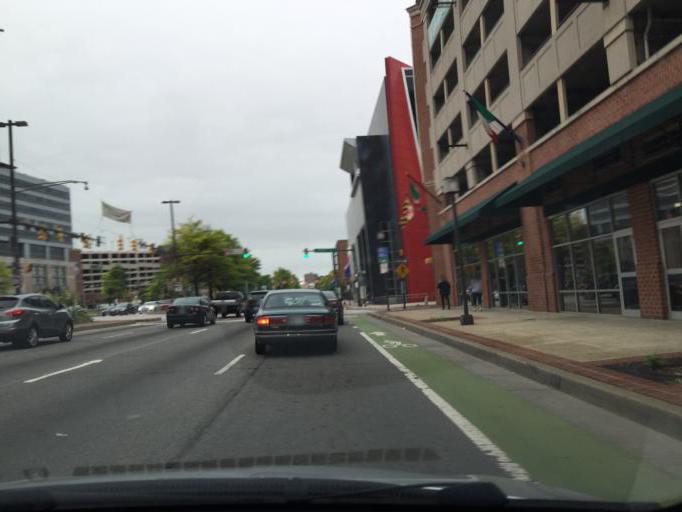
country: US
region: Maryland
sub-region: City of Baltimore
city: Baltimore
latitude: 39.2865
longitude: -76.6036
